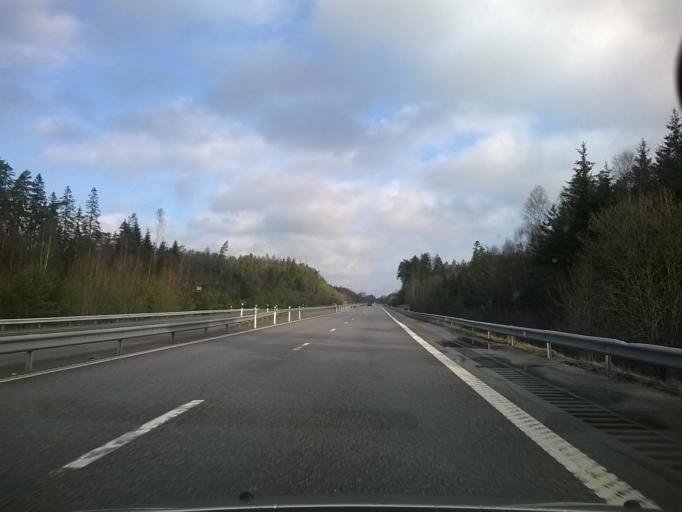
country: SE
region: Vaestra Goetaland
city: Svanesund
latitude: 58.1371
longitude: 11.8856
